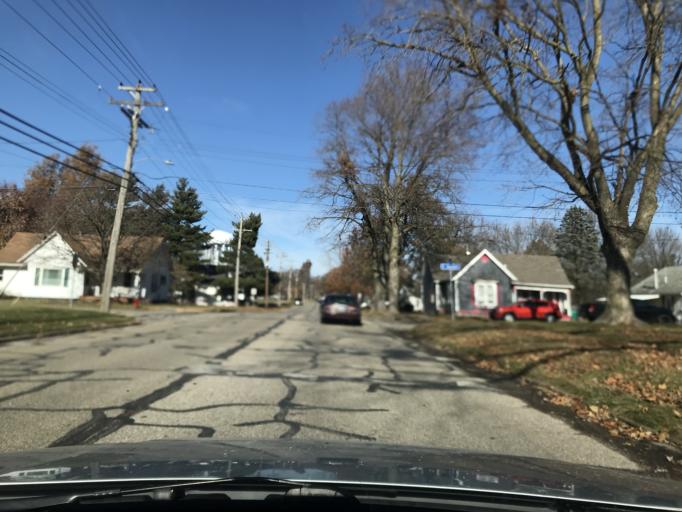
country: US
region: Illinois
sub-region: McDonough County
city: Macomb
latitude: 40.4495
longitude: -90.6674
